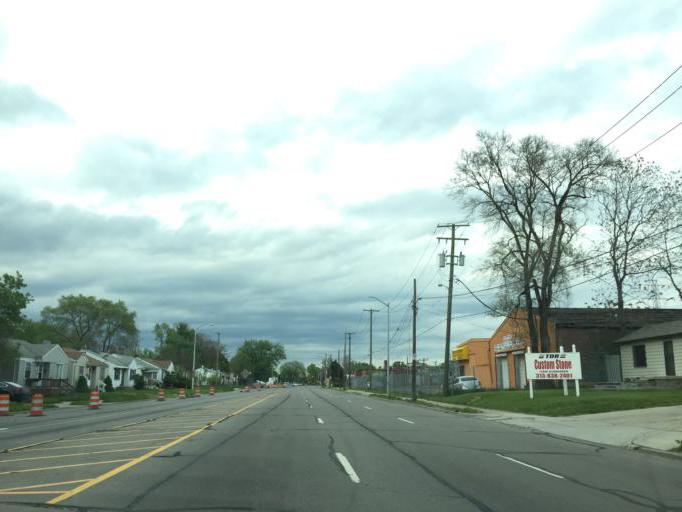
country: US
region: Michigan
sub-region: Wayne County
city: Dearborn Heights
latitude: 42.3827
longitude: -83.2367
